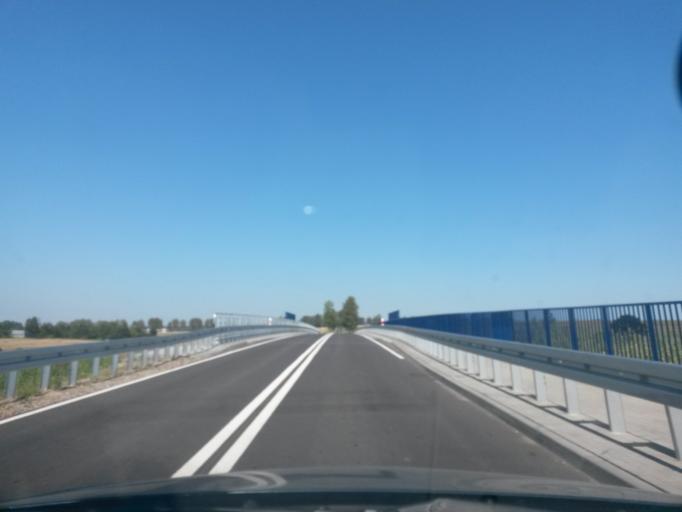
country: PL
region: Warmian-Masurian Voivodeship
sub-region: Powiat ilawski
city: Lubawa
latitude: 53.4098
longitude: 19.7948
